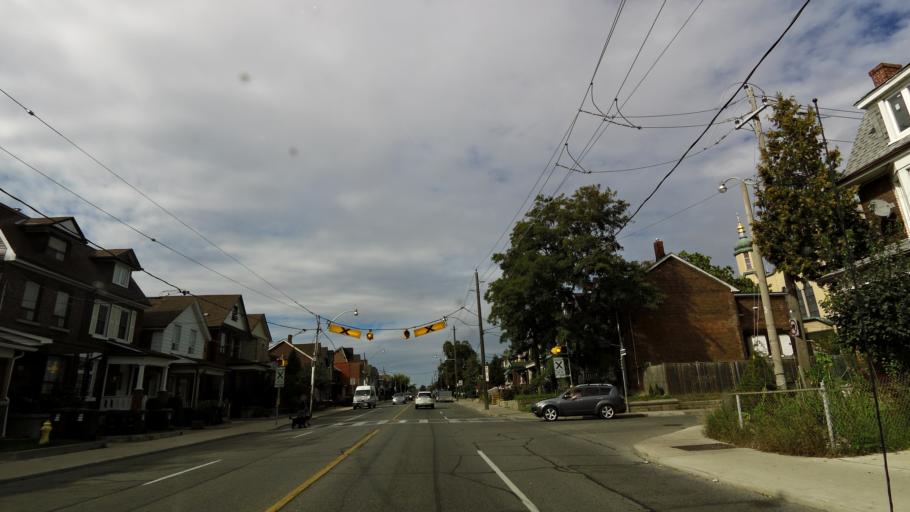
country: CA
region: Ontario
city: Toronto
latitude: 43.6639
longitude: -79.4265
